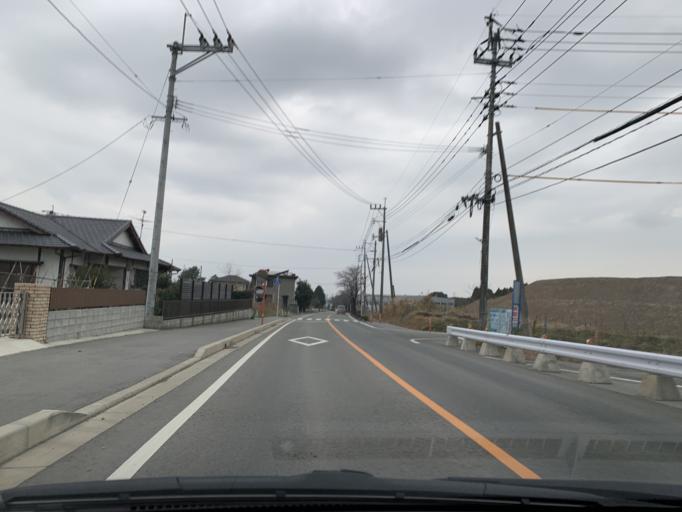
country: JP
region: Kumamoto
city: Ozu
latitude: 32.8901
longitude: 130.8961
